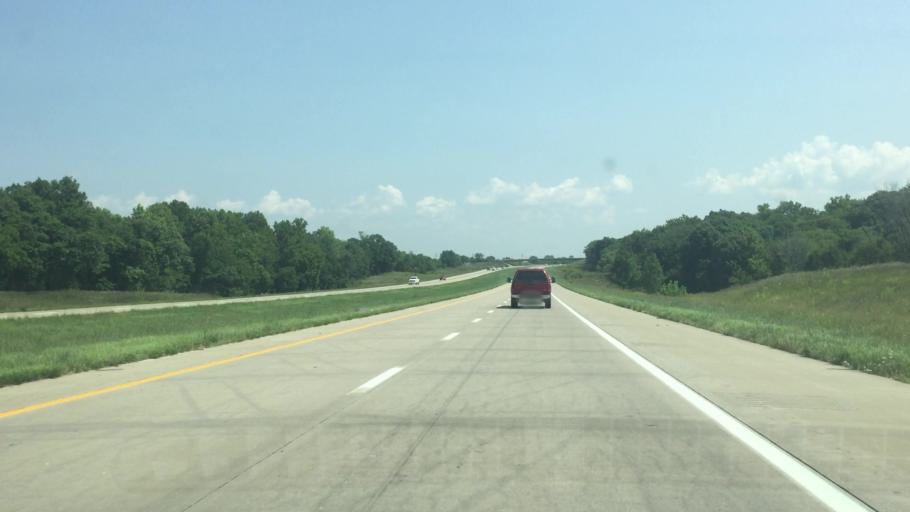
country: US
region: Kansas
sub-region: Franklin County
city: Ottawa
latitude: 38.5434
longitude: -95.3685
